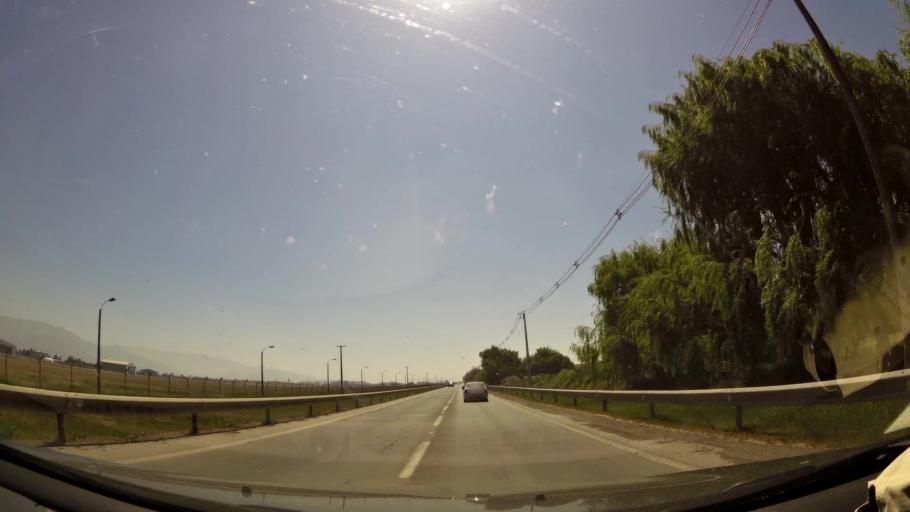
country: CL
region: Santiago Metropolitan
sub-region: Provincia de Santiago
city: Lo Prado
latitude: -33.3875
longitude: -70.7838
